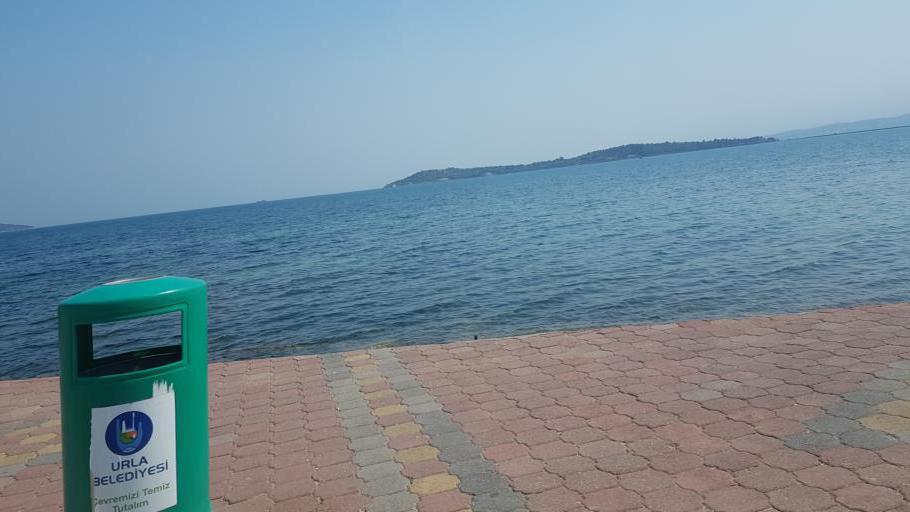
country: TR
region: Izmir
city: Urla
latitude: 38.3684
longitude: 26.7642
